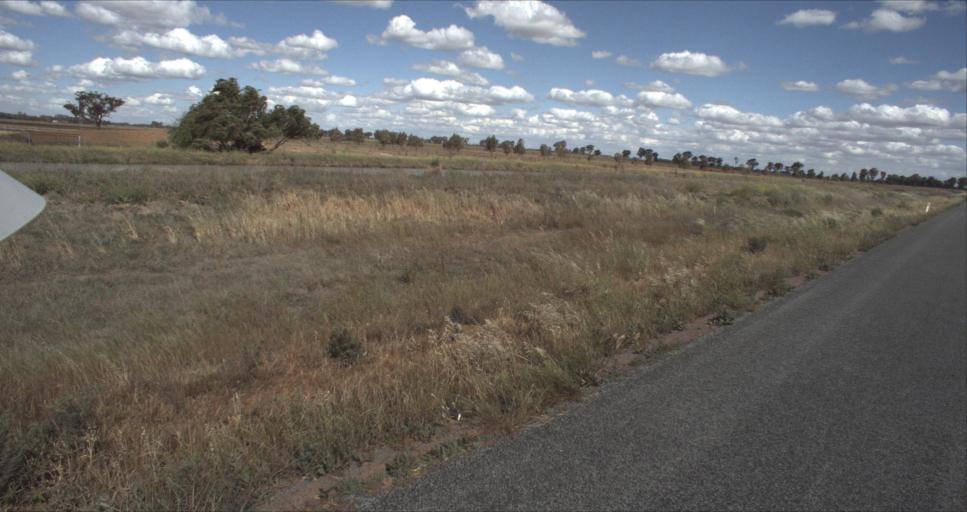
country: AU
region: New South Wales
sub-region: Leeton
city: Leeton
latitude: -34.4521
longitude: 146.2544
